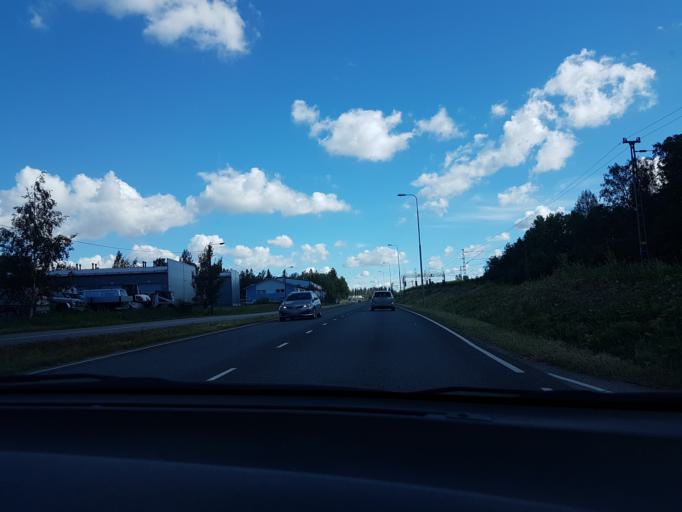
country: FI
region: Uusimaa
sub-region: Helsinki
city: Kerava
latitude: 60.3691
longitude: 25.0915
